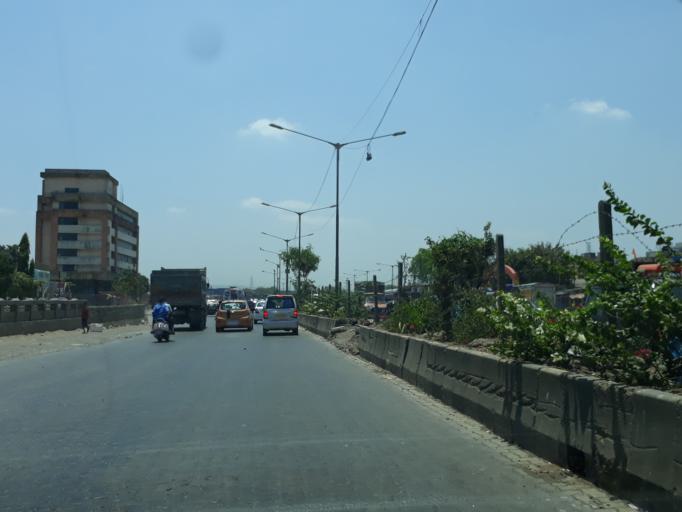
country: IN
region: Maharashtra
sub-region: Mumbai Suburban
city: Mumbai
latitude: 19.0566
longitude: 72.9292
